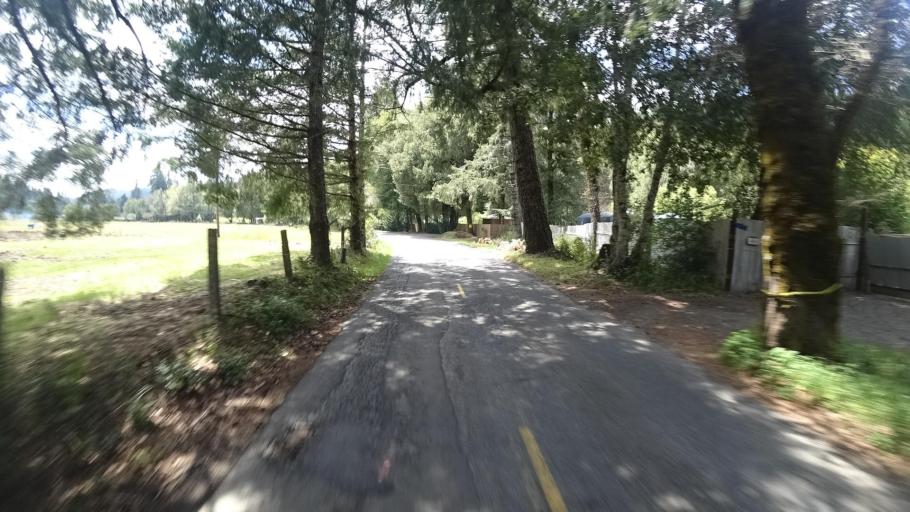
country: US
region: California
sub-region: Humboldt County
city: Redway
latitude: 40.0432
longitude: -123.9593
